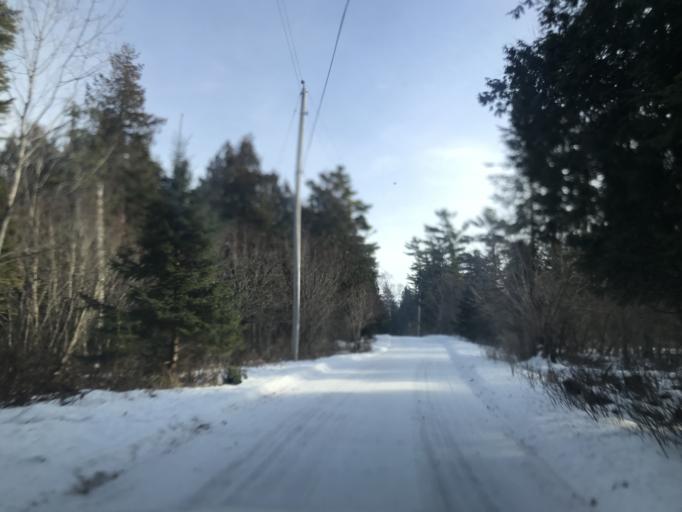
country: US
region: Wisconsin
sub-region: Door County
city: Sturgeon Bay
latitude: 45.1493
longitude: -87.0362
